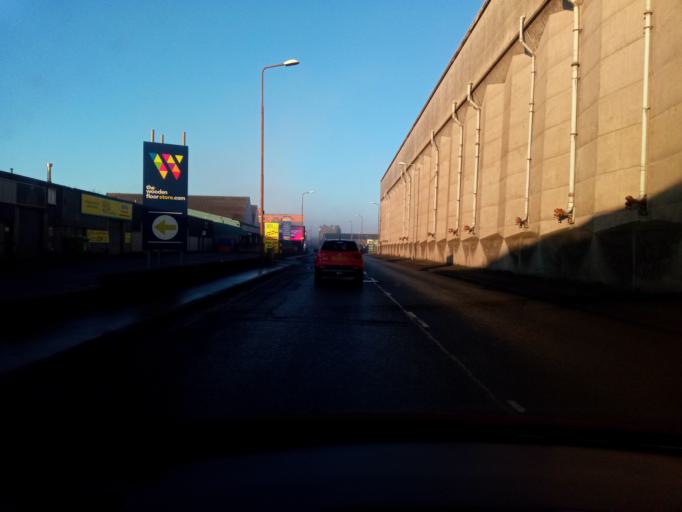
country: GB
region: Scotland
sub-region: West Lothian
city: Seafield
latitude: 55.9727
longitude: -3.1554
